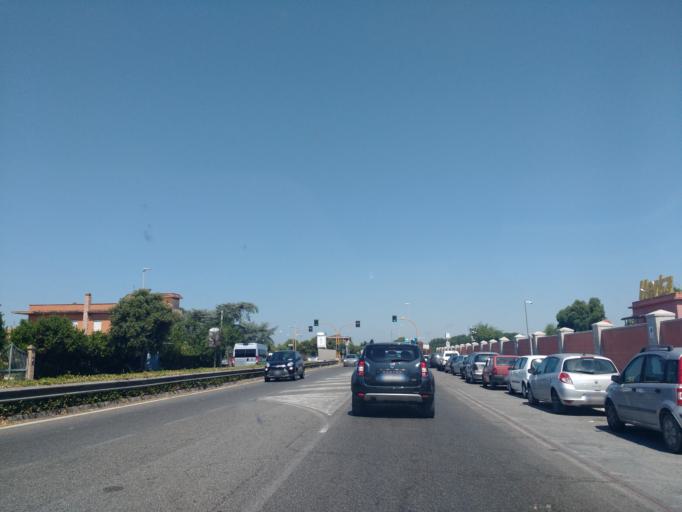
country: IT
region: Latium
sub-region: Citta metropolitana di Roma Capitale
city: Fiumicino-Isola Sacra
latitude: 41.7652
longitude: 12.2641
